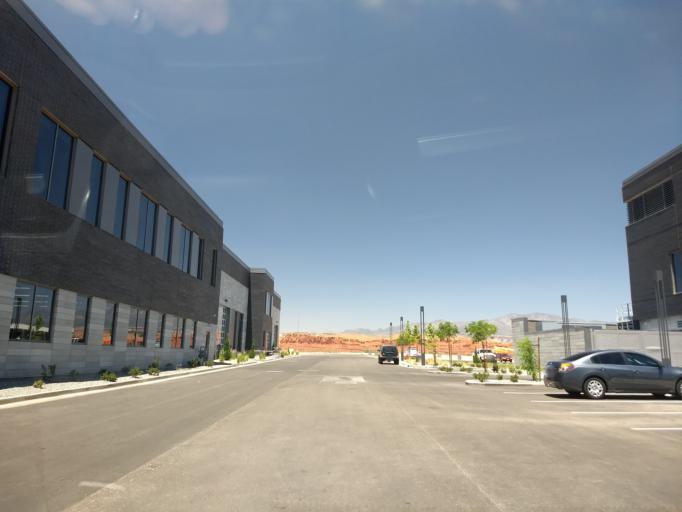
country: US
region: Utah
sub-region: Washington County
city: Saint George
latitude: 37.0983
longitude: -113.5924
